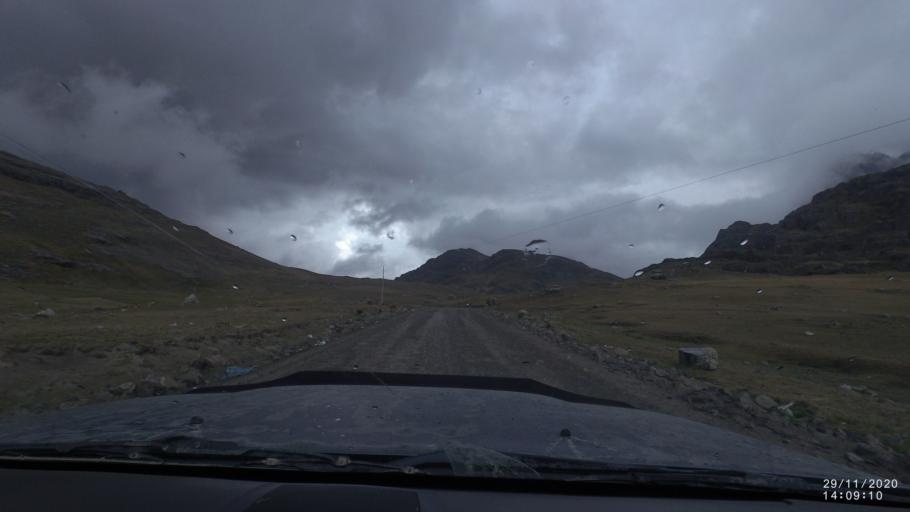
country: BO
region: Cochabamba
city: Sipe Sipe
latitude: -17.2257
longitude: -66.3841
